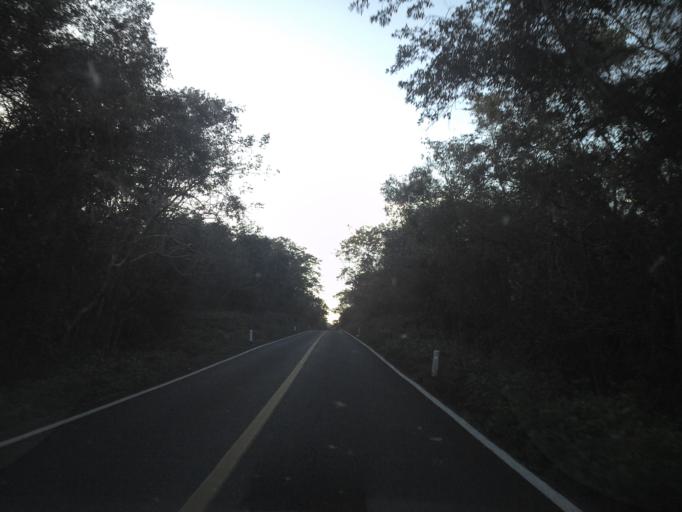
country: MX
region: Yucatan
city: Santa Elena
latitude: 20.3395
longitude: -89.6895
